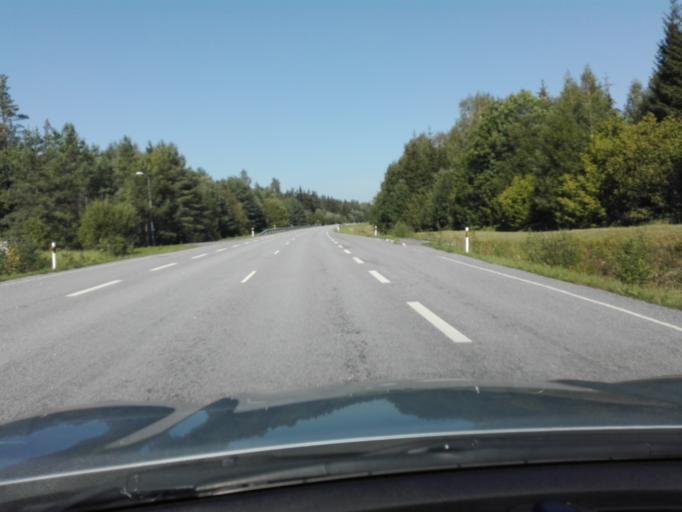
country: EE
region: Raplamaa
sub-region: Rapla vald
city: Rapla
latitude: 59.0043
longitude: 24.7689
